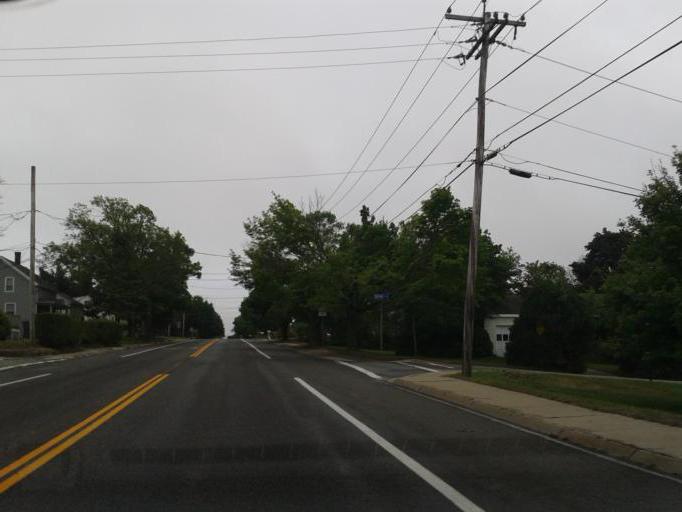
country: US
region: Rhode Island
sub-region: Newport County
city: Portsmouth
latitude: 41.6086
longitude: -71.2535
